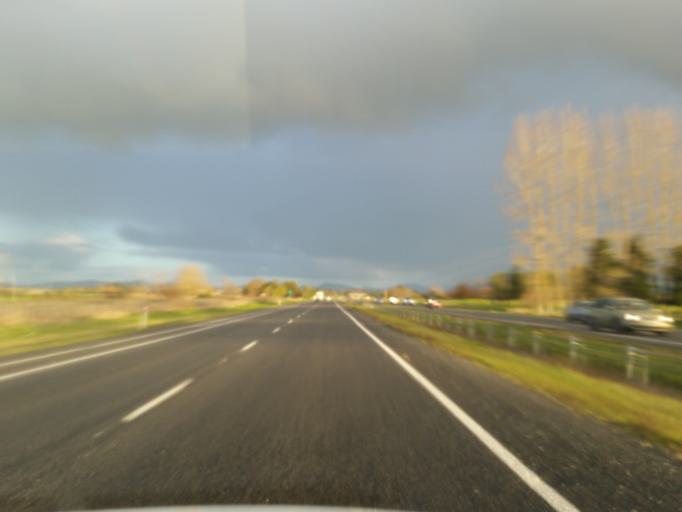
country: NZ
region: Waikato
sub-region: Waikato District
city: Te Kauwhata
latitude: -37.4768
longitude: 175.1597
